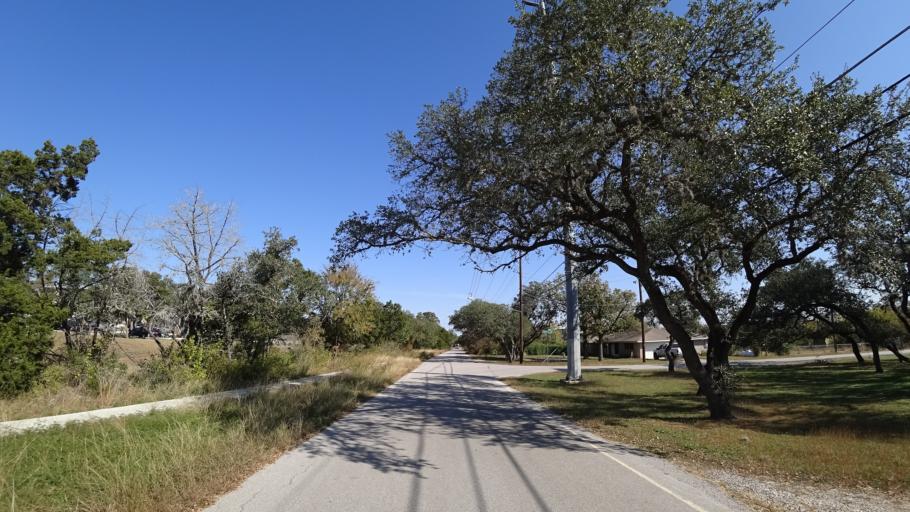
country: US
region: Texas
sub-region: Travis County
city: Barton Creek
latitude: 30.2305
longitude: -97.8593
